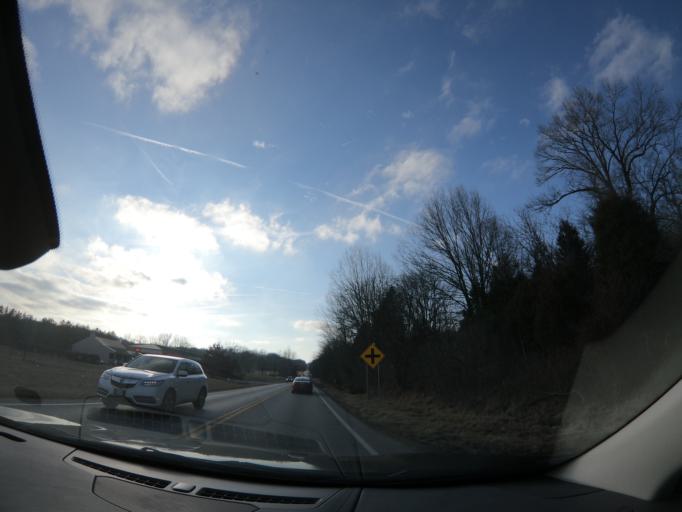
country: US
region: Kentucky
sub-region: Jefferson County
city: Middletown
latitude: 38.1909
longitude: -85.4850
